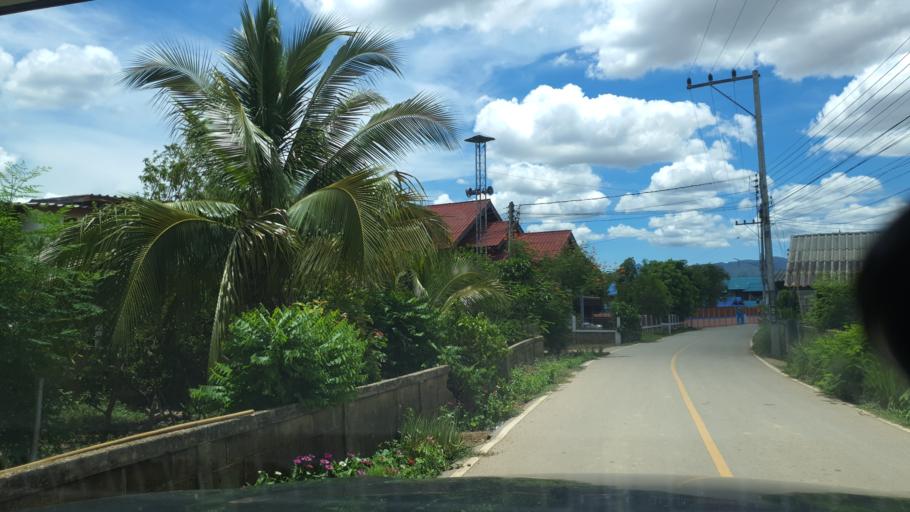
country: TH
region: Lampang
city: Sop Prap
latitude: 17.9433
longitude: 99.3418
